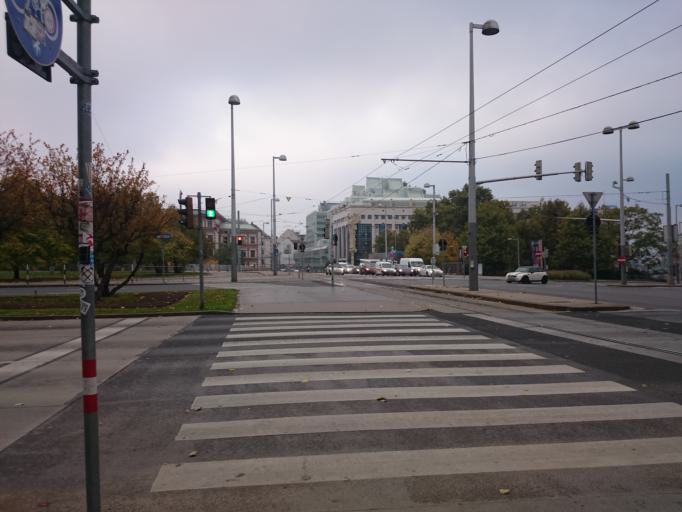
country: AT
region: Vienna
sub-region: Wien Stadt
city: Vienna
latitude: 48.2010
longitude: 16.3692
